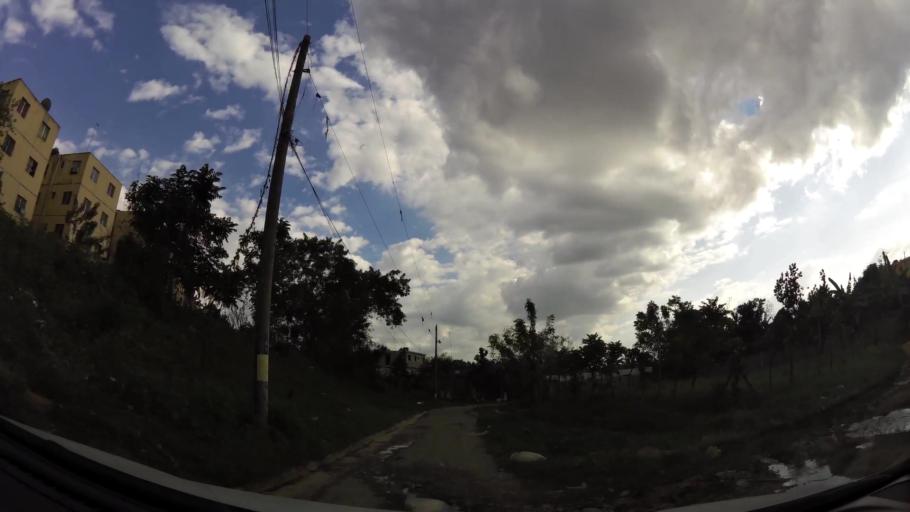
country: DO
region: Nacional
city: Ensanche Luperon
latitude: 18.5624
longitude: -69.9112
